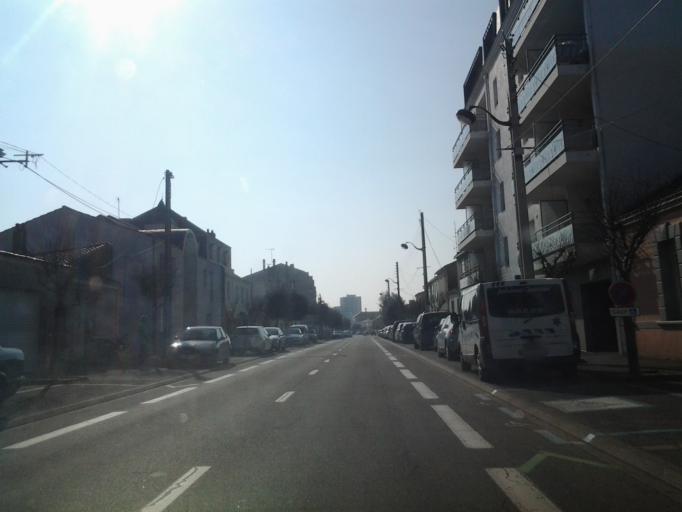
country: FR
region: Pays de la Loire
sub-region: Departement de la Vendee
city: Les Sables-d'Olonne
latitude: 46.5030
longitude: -1.7756
